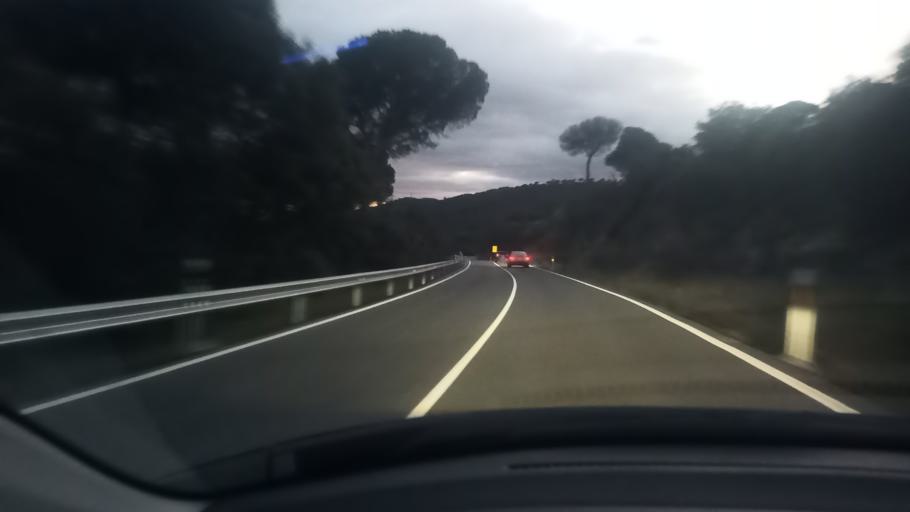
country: ES
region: Madrid
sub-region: Provincia de Madrid
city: Robledo de Chavela
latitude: 40.4466
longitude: -4.2643
